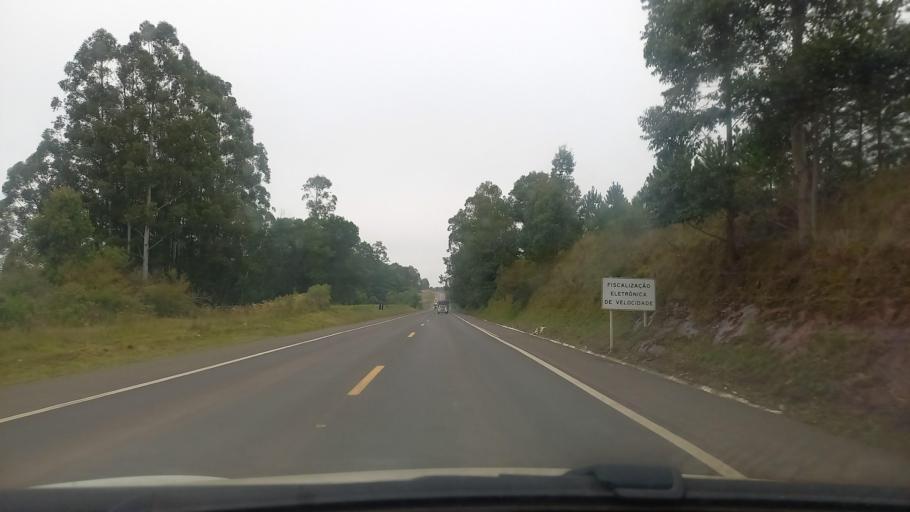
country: BR
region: Rio Grande do Sul
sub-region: Rosario Do Sul
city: Rosario do Sul
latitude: -30.2609
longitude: -54.9675
